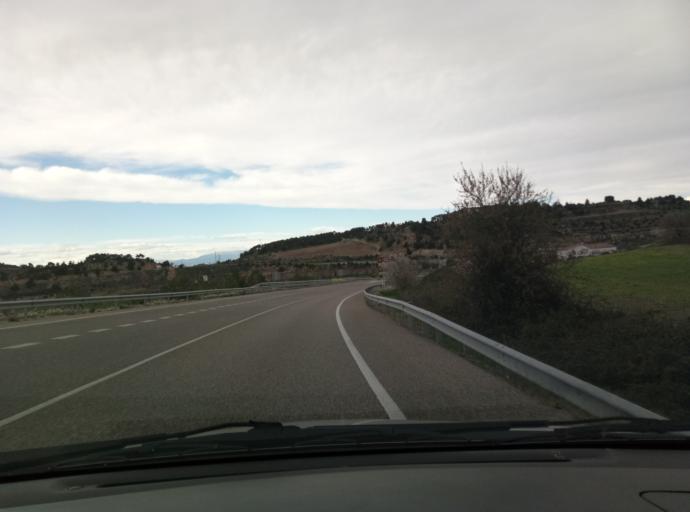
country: ES
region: Catalonia
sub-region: Provincia de Lleida
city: Ciutadilla
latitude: 41.5624
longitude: 1.1290
